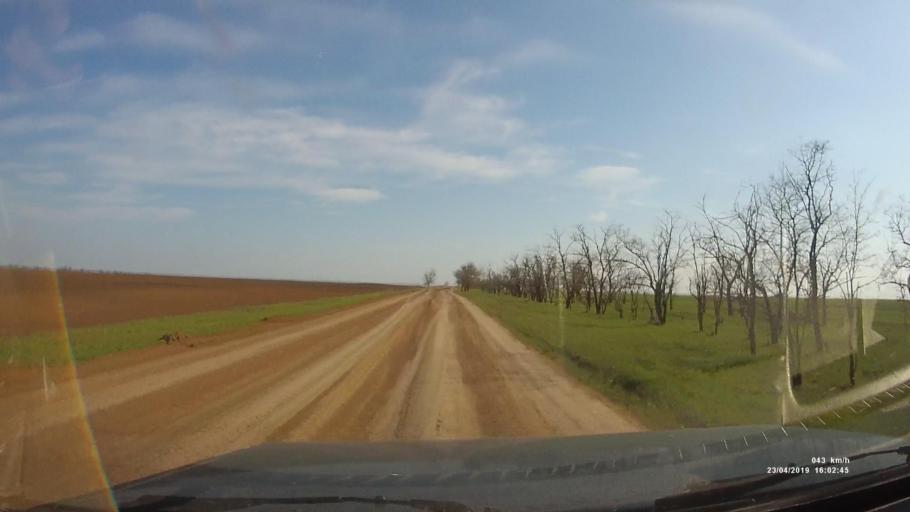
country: RU
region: Rostov
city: Remontnoye
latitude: 46.4920
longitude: 43.1071
